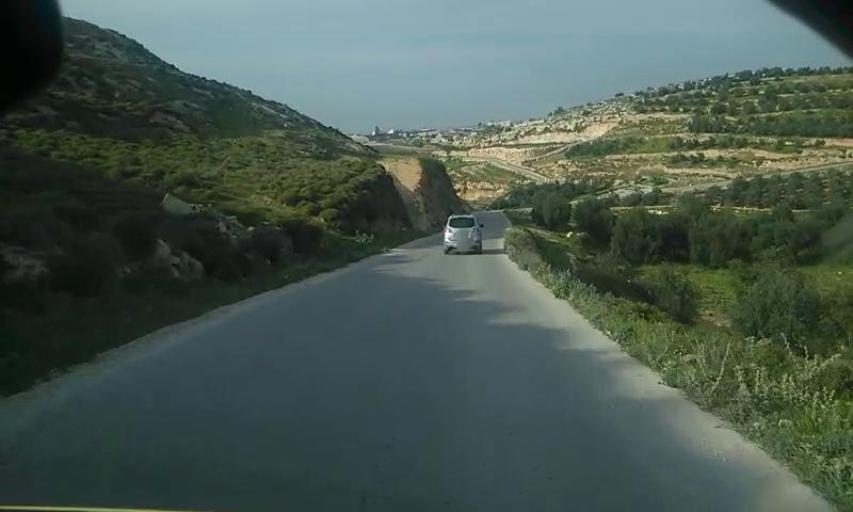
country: PS
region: West Bank
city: Nuba
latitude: 31.6126
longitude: 35.0185
